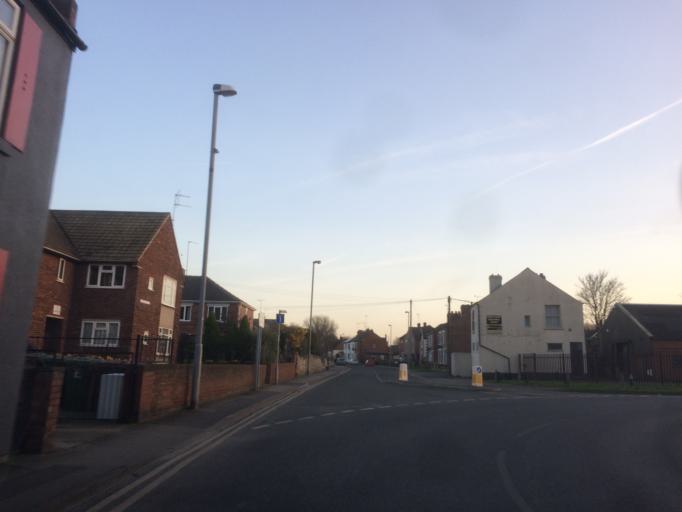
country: GB
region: England
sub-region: City and Borough of Wakefield
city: Ferrybridge
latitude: 53.7122
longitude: -1.2681
